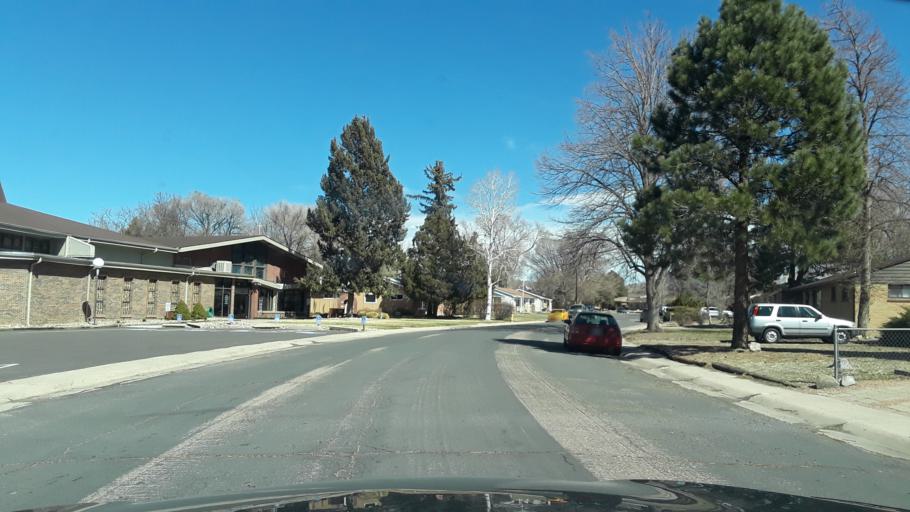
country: US
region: Colorado
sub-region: El Paso County
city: Colorado Springs
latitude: 38.8755
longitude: -104.8001
